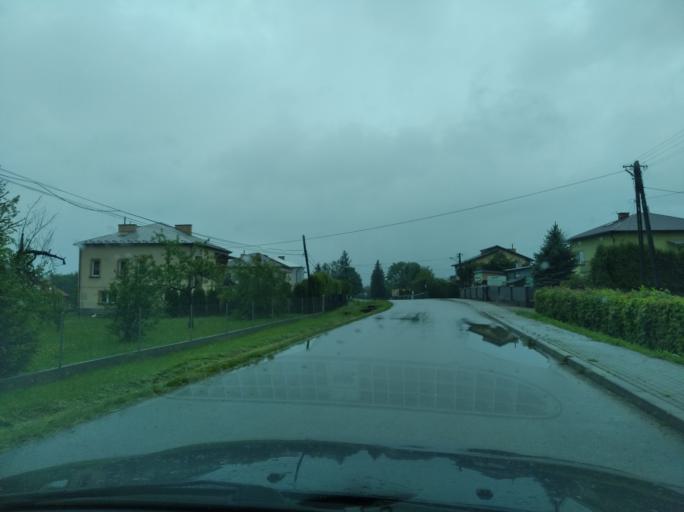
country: PL
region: Subcarpathian Voivodeship
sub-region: Powiat jasielski
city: Tarnowiec
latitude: 49.7670
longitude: 21.5416
